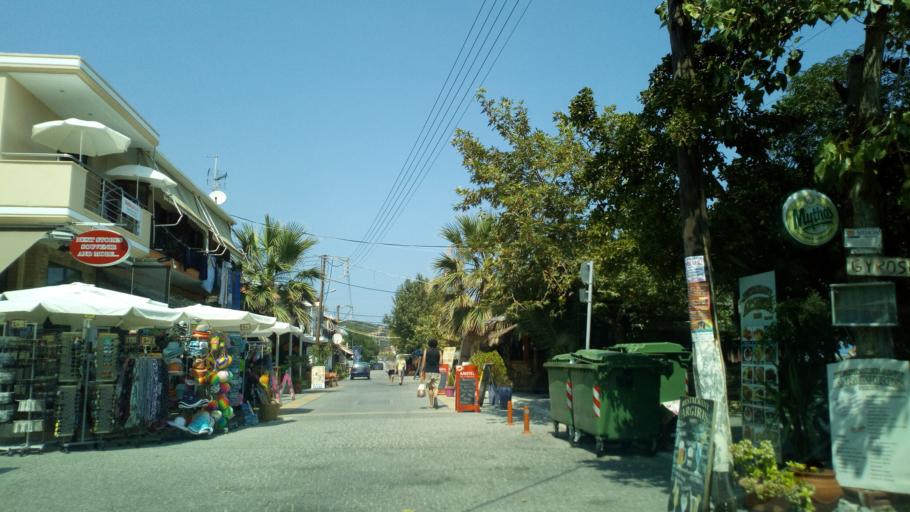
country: GR
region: Central Macedonia
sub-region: Nomos Chalkidikis
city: Sarti
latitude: 40.0956
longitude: 23.9794
